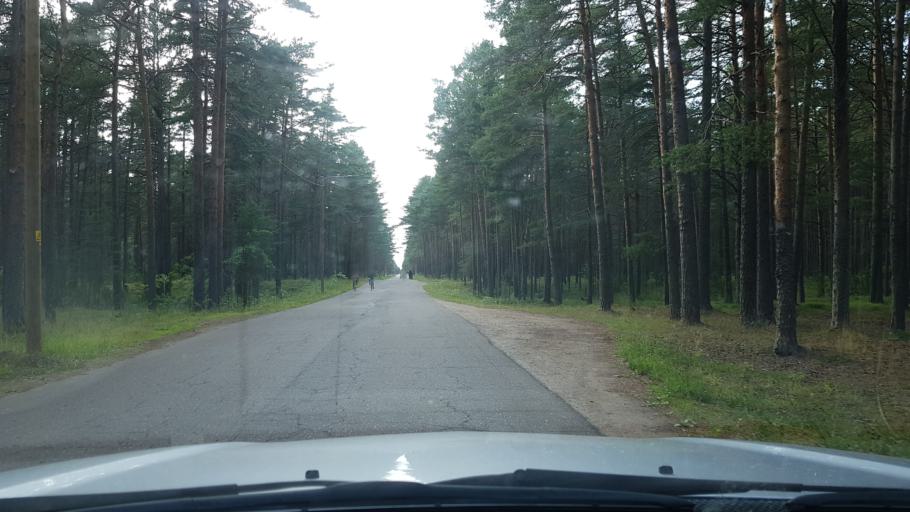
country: EE
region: Ida-Virumaa
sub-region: Narva-Joesuu linn
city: Narva-Joesuu
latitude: 59.4497
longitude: 28.0652
